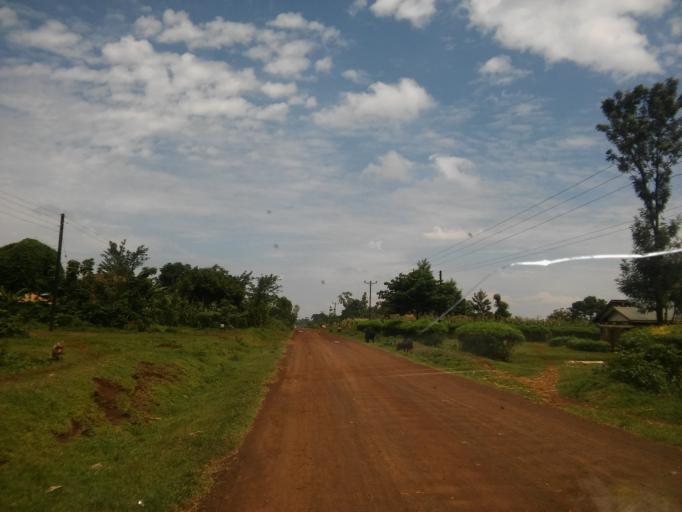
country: UG
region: Eastern Region
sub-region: Bududa District
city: Bududa
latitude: 0.8909
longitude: 34.2632
